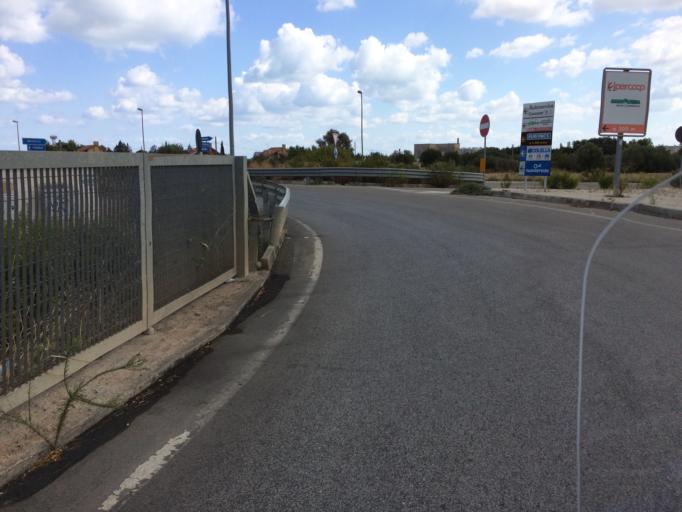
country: IT
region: Apulia
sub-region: Provincia di Bari
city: Modugno
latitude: 41.0940
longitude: 16.8278
